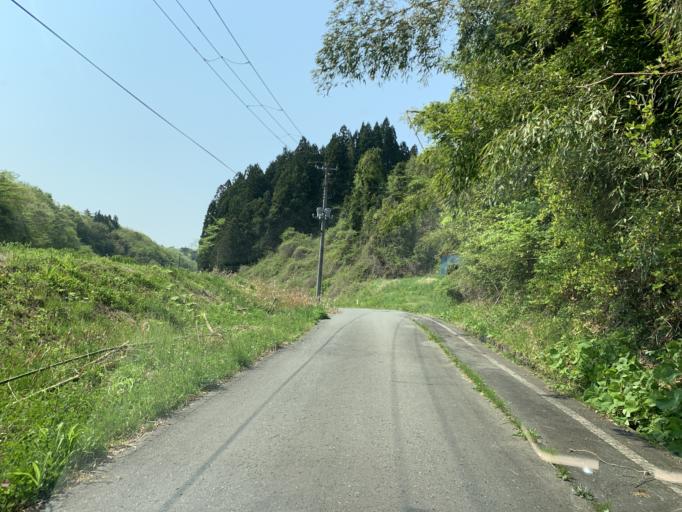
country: JP
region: Iwate
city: Ichinoseki
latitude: 38.8923
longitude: 141.1019
